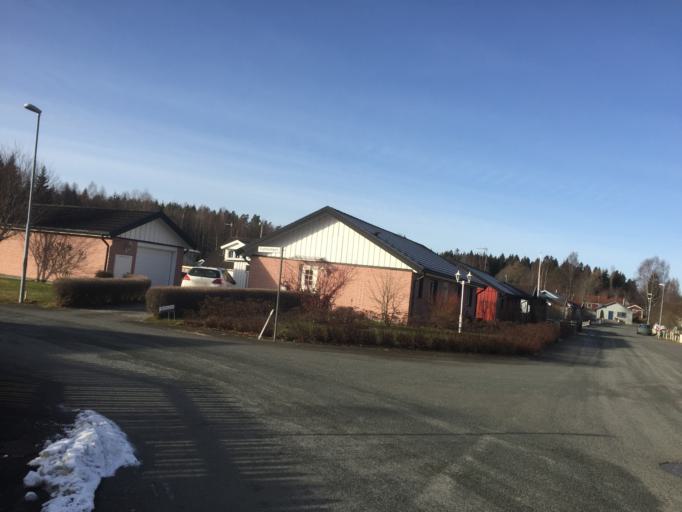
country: SE
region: Joenkoeping
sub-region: Aneby Kommun
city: Aneby
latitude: 57.8466
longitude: 14.7962
